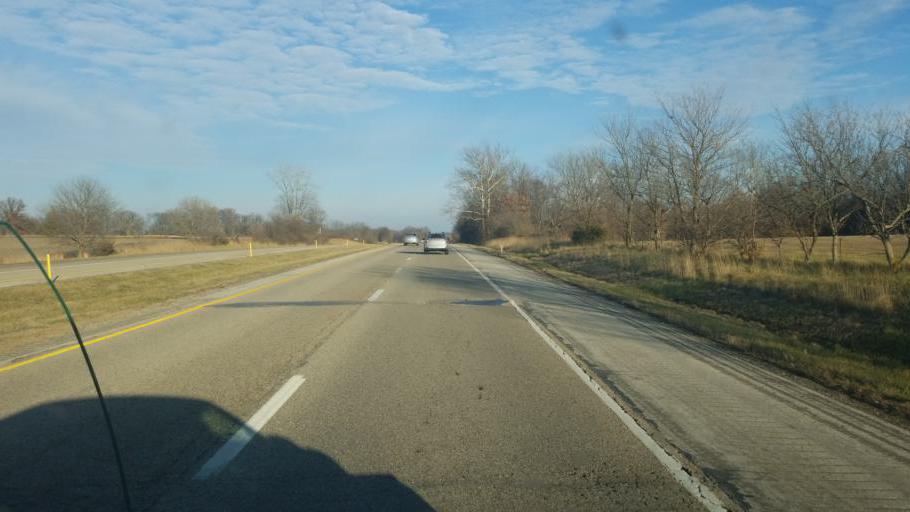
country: US
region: Indiana
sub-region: Knox County
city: Vincennes
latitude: 38.6776
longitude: -87.4195
